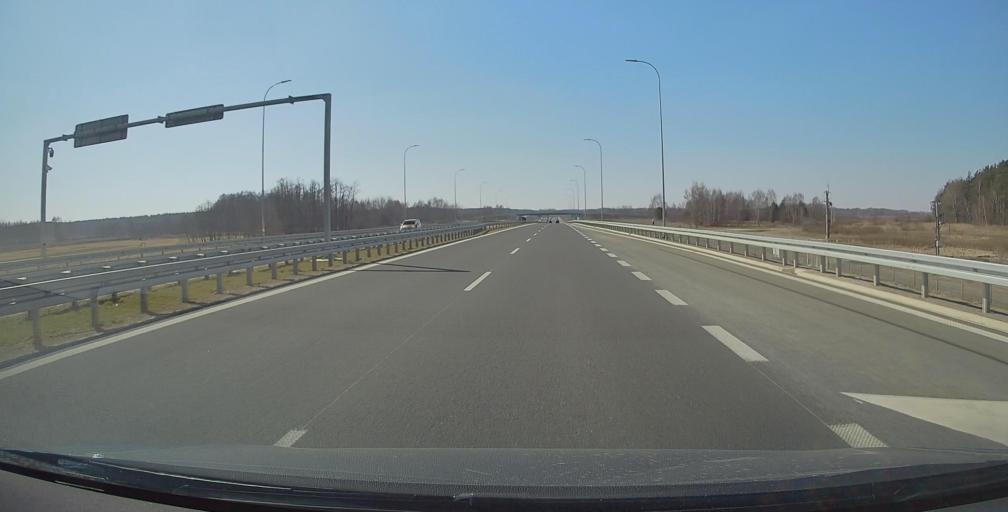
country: PL
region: Subcarpathian Voivodeship
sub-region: Powiat lezajski
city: Letownia
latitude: 50.3299
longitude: 22.1902
